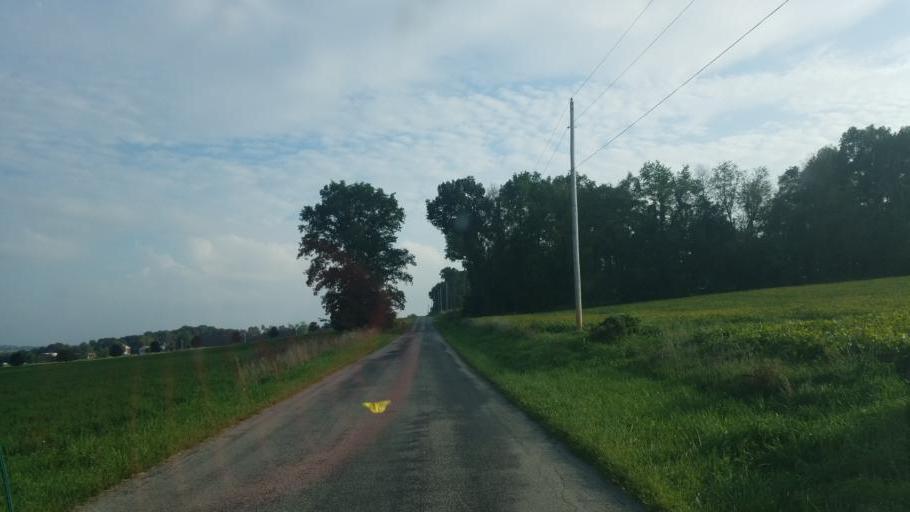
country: US
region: Ohio
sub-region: Wayne County
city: West Salem
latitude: 40.8955
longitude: -82.0236
